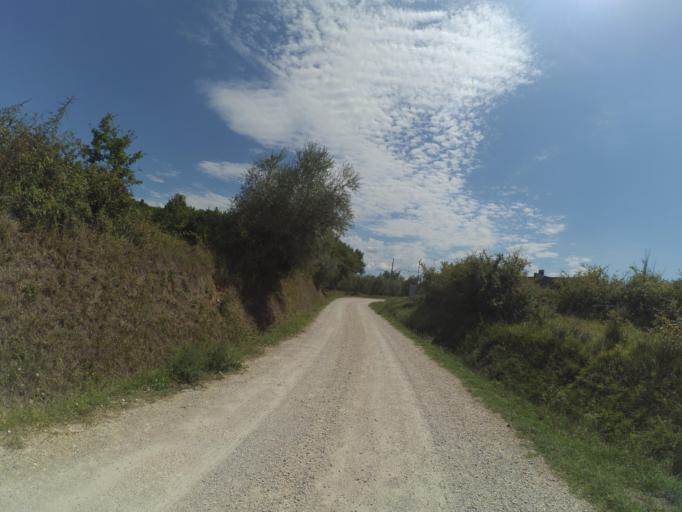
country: IT
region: Tuscany
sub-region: Province of Arezzo
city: Castiglion Fibocchi
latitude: 43.5320
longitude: 11.7660
